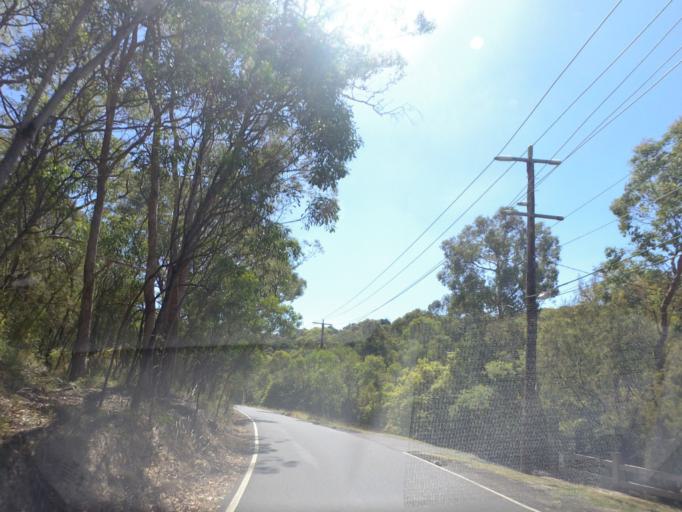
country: AU
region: Victoria
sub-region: Manningham
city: Park Orchards
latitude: -37.7910
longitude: 145.2182
